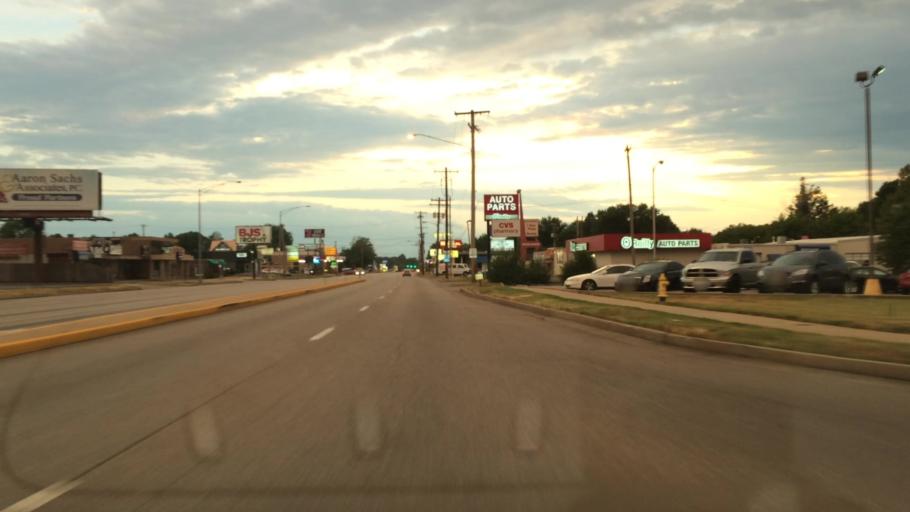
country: US
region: Missouri
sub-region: Greene County
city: Springfield
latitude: 37.1818
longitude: -93.2626
